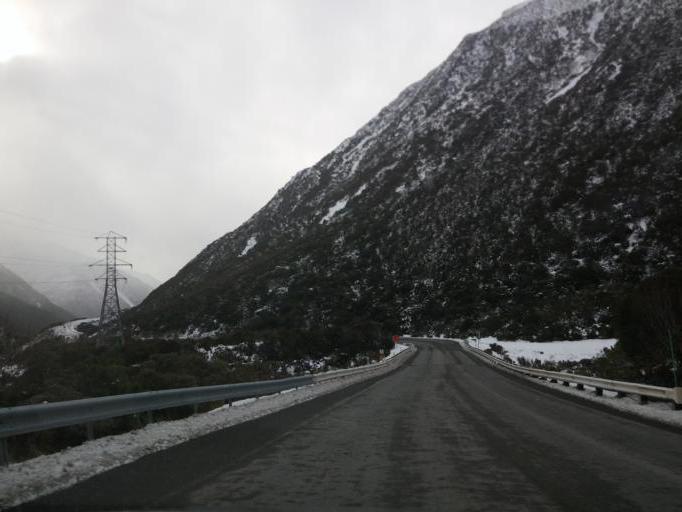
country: NZ
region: West Coast
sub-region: Grey District
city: Greymouth
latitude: -42.8956
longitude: 171.5586
